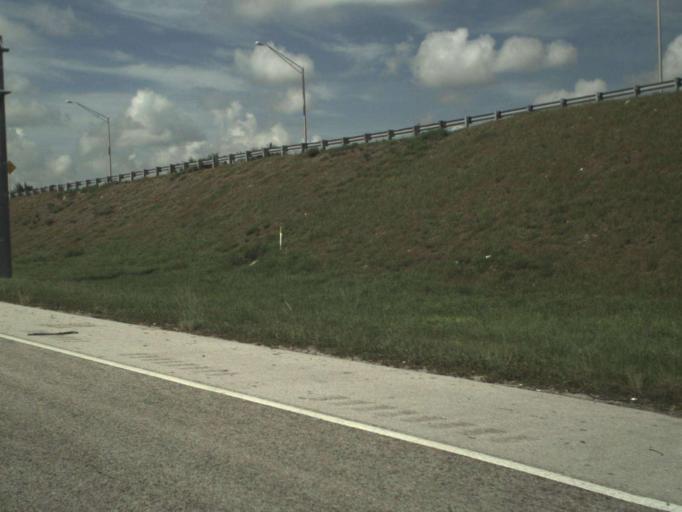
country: US
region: Florida
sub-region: Palm Beach County
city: Lake Clarke Shores
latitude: 26.6751
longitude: -80.0700
